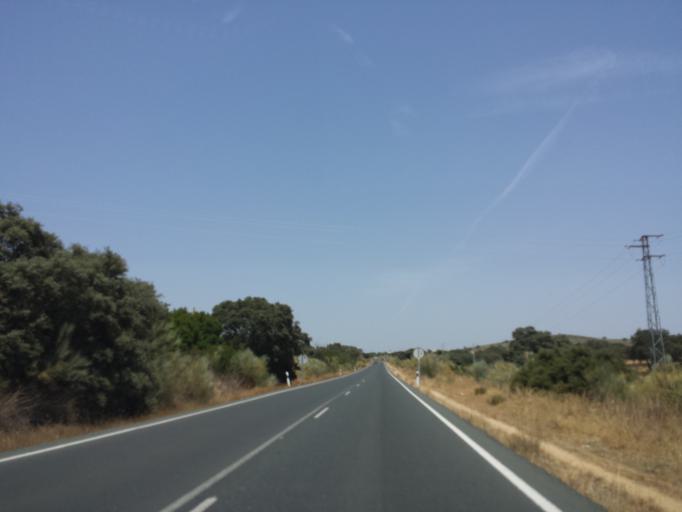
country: ES
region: Andalusia
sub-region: Provincia de Sevilla
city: Castilblanco de los Arroyos
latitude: 37.6531
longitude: -6.0084
